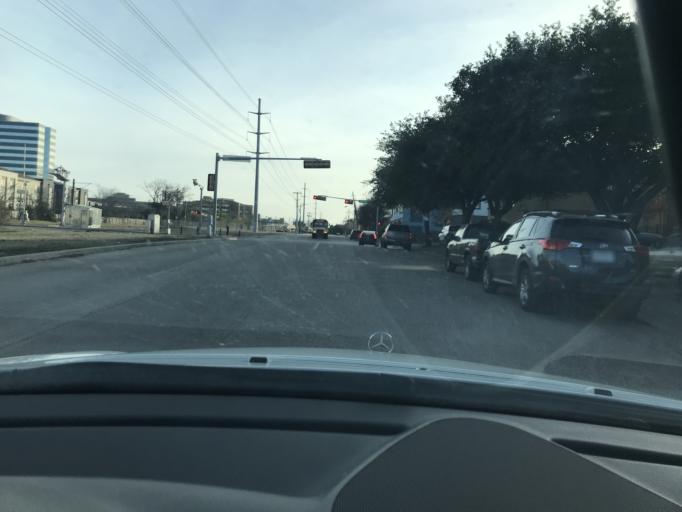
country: US
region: Texas
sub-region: Dallas County
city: University Park
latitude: 32.8881
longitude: -96.7653
